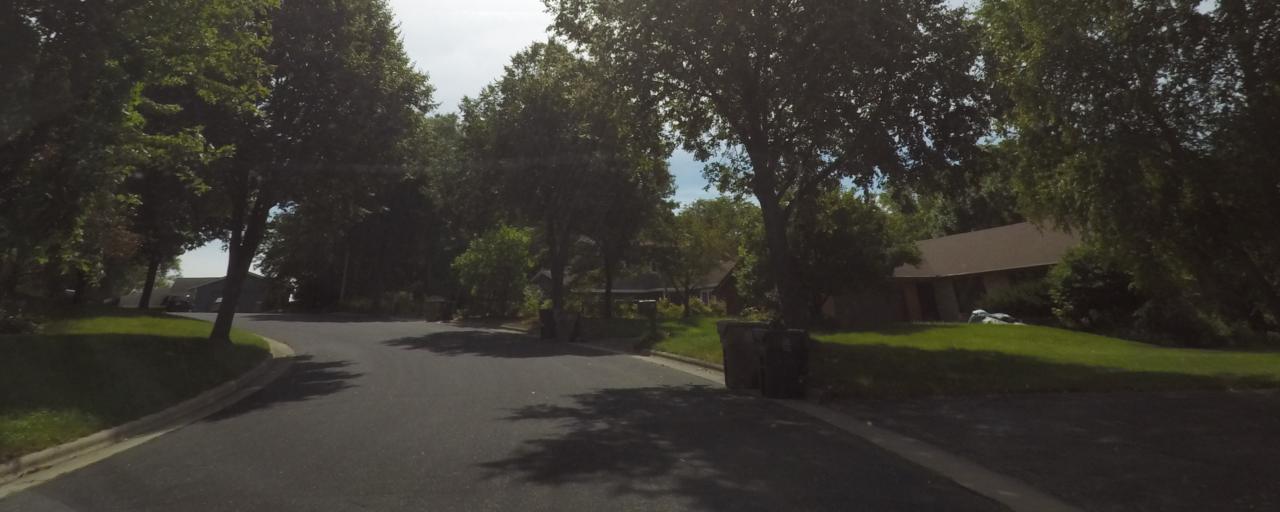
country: US
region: Wisconsin
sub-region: Dane County
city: Middleton
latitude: 43.0857
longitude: -89.4868
